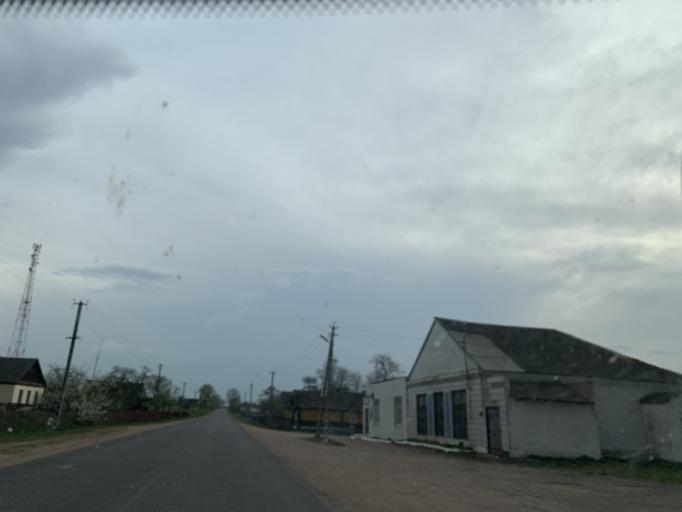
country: BY
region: Minsk
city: Kapyl'
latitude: 53.2793
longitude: 26.9754
